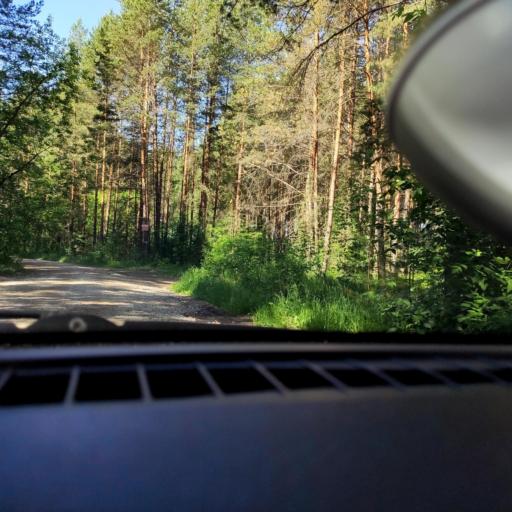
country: RU
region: Perm
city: Overyata
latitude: 58.0087
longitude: 55.8738
